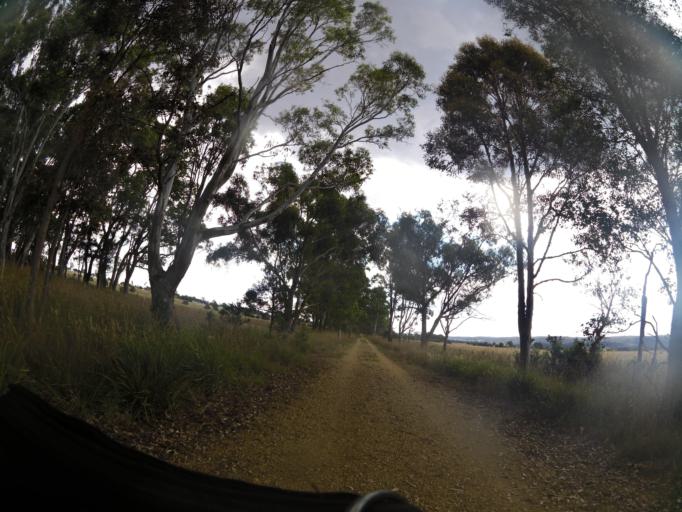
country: AU
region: Victoria
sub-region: Wellington
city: Heyfield
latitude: -38.0176
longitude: 146.6862
